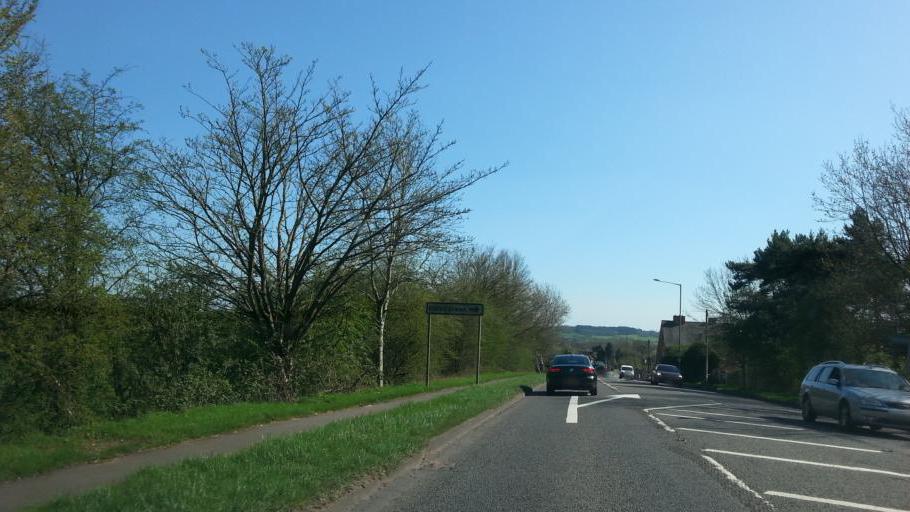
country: GB
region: England
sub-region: Worcestershire
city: Alvechurch
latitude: 52.3736
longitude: -1.9570
